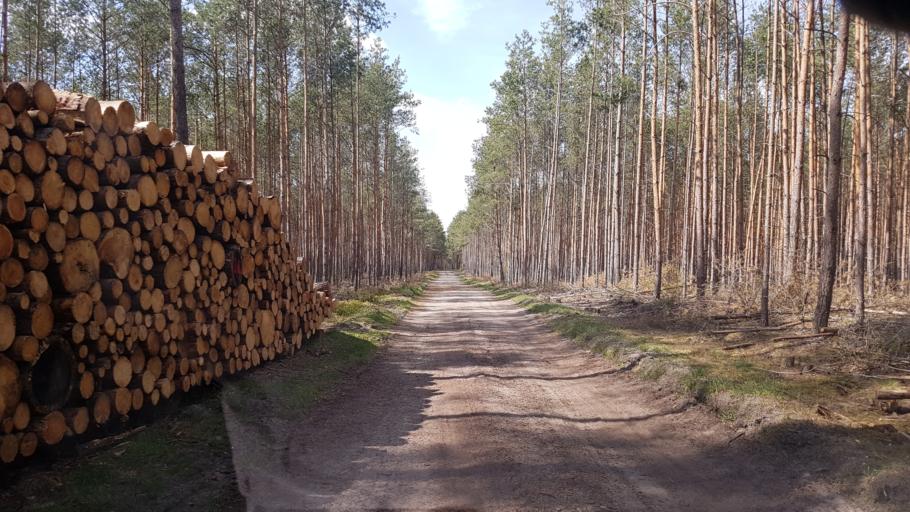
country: DE
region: Brandenburg
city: Ruckersdorf
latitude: 51.5507
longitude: 13.6385
